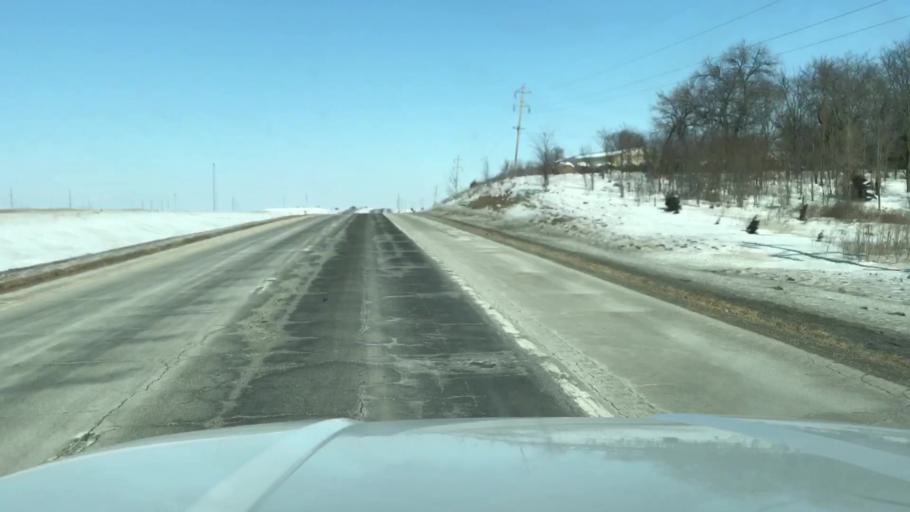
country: US
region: Missouri
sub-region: Nodaway County
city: Maryville
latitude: 40.2178
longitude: -94.8678
